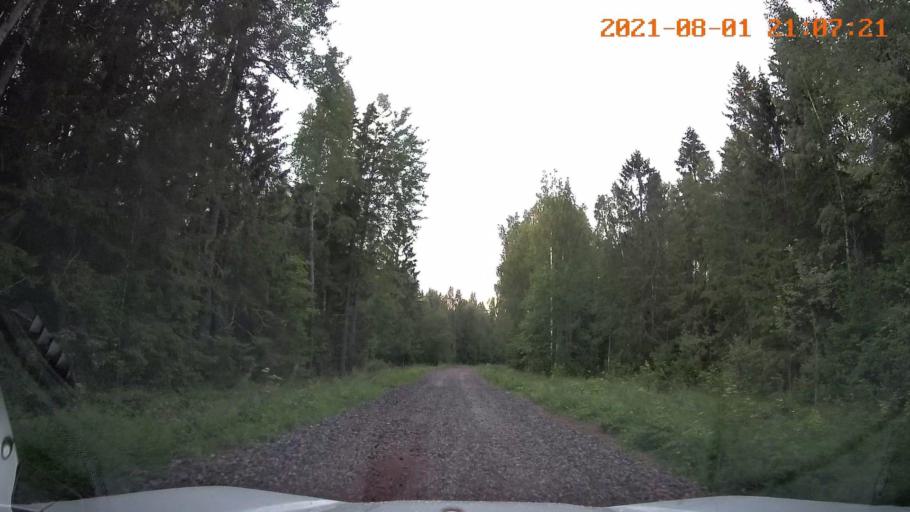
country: RU
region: Leningrad
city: Syas'stroy
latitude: 60.5040
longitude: 32.6493
